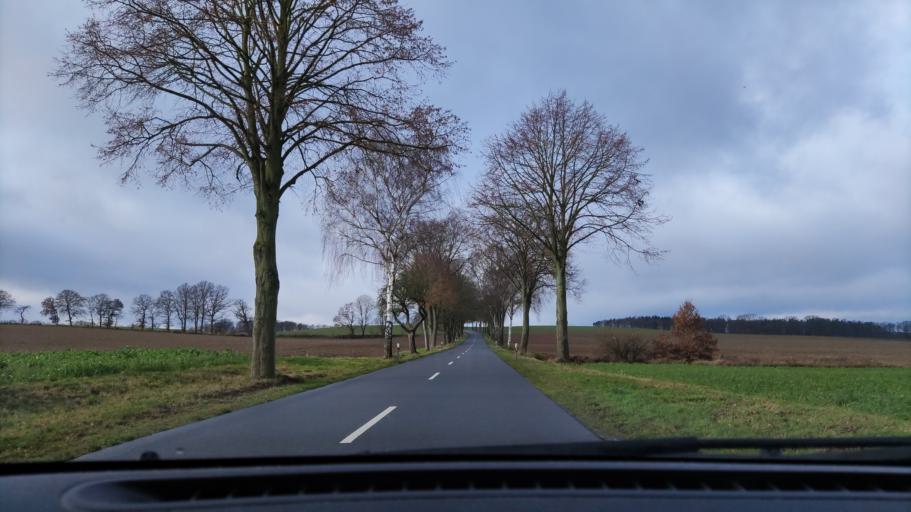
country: DE
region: Lower Saxony
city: Jelmstorf
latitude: 53.0806
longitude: 10.5027
